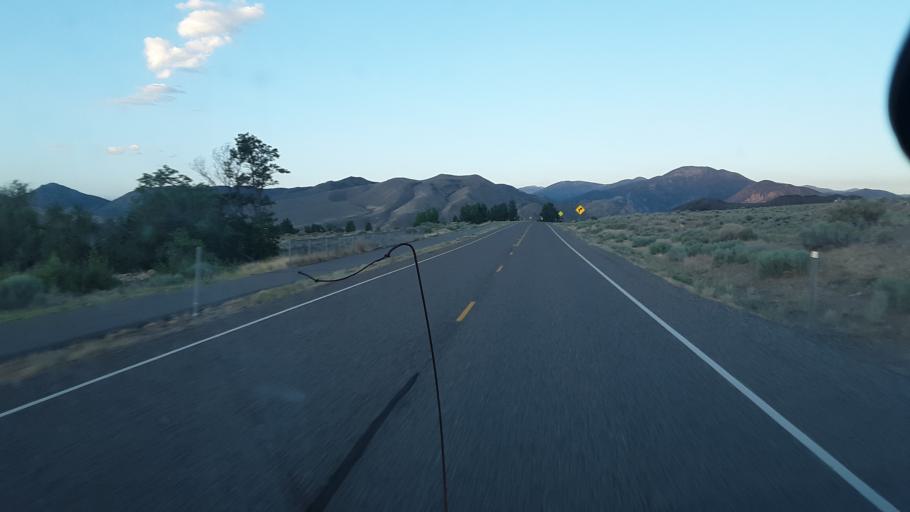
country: US
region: Utah
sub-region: Sevier County
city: Monroe
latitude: 38.6082
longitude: -112.2260
